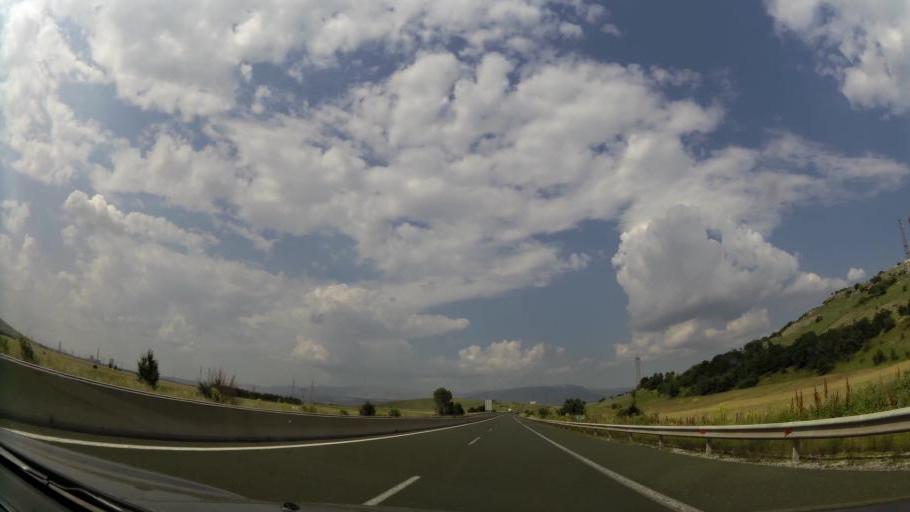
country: GR
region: West Macedonia
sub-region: Nomos Kozanis
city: Koila
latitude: 40.3563
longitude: 21.8136
